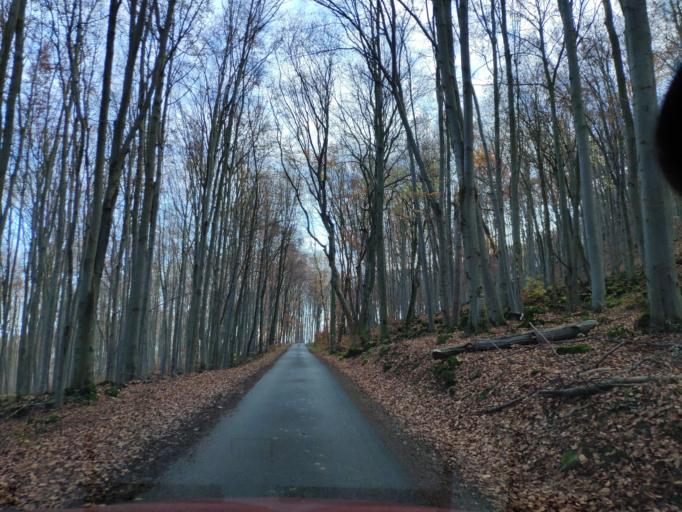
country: HU
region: Borsod-Abauj-Zemplen
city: Gonc
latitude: 48.5872
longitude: 21.4645
